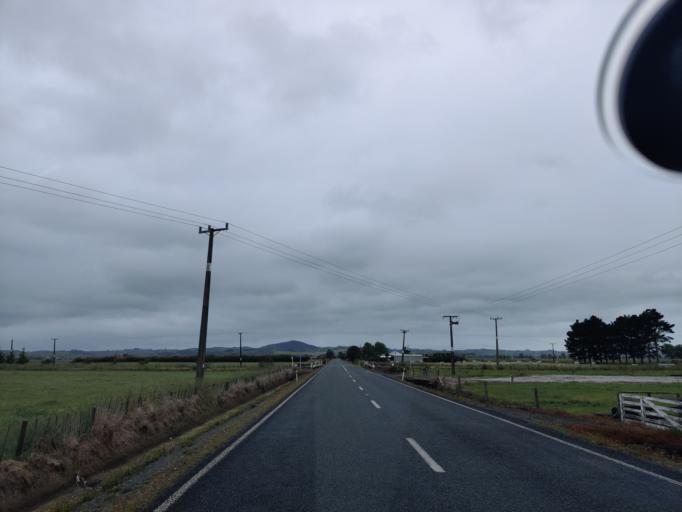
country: NZ
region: Northland
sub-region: Kaipara District
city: Dargaville
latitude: -36.1237
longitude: 174.0493
